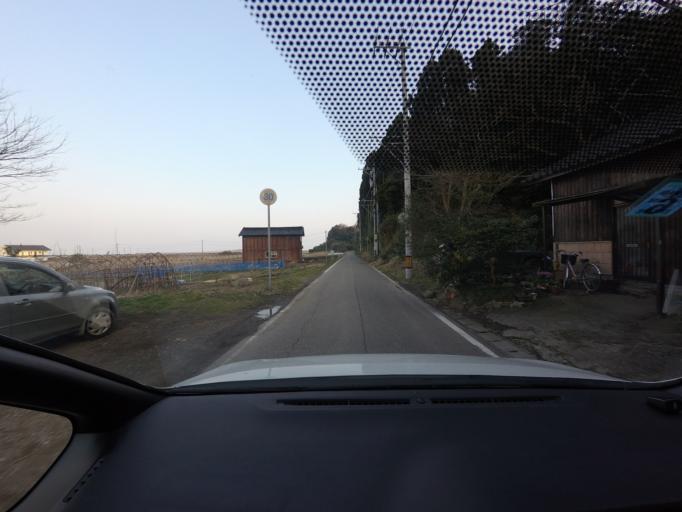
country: JP
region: Ishikawa
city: Nanao
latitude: 37.1676
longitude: 137.0386
